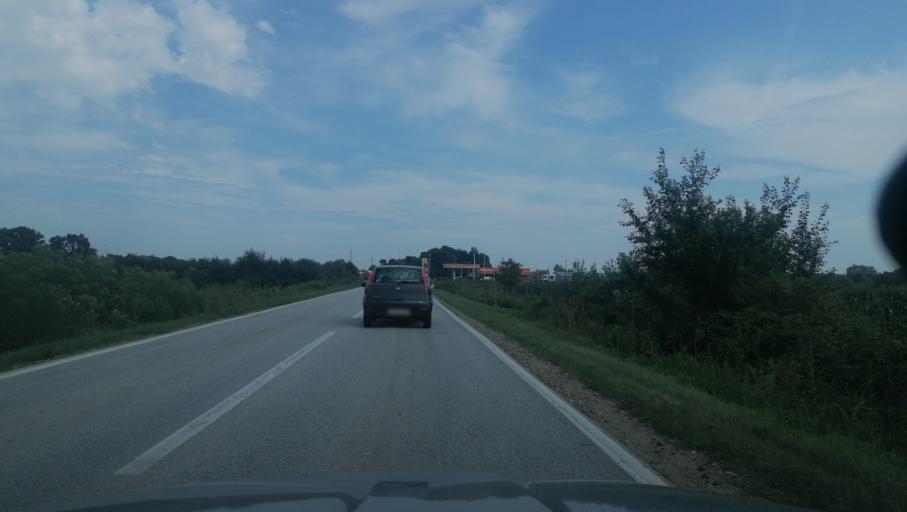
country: HR
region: Vukovarsko-Srijemska
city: Soljani
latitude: 44.8296
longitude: 19.0111
